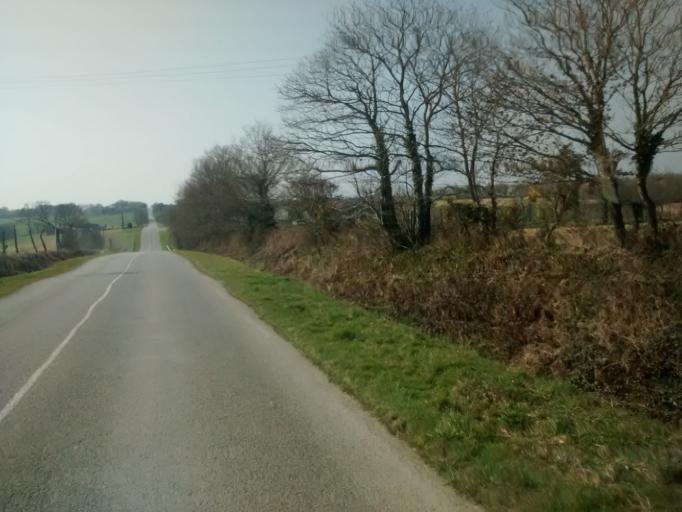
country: FR
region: Brittany
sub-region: Departement d'Ille-et-Vilaine
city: Maxent
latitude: 48.0241
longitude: -2.0335
